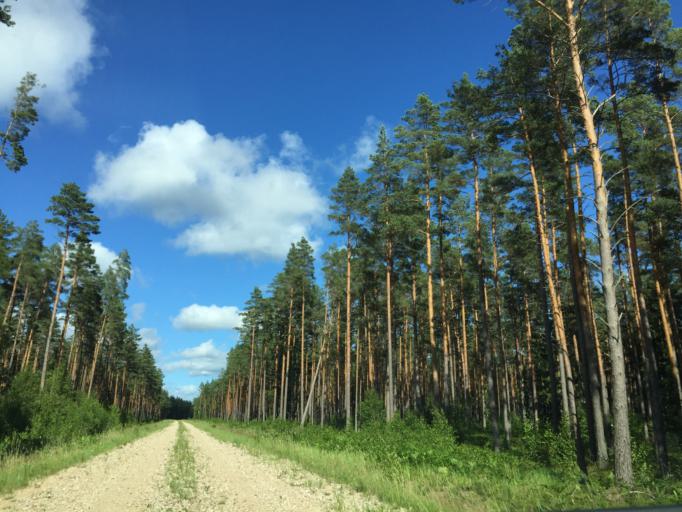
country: LV
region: Ventspils
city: Ventspils
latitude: 57.5344
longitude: 21.7266
